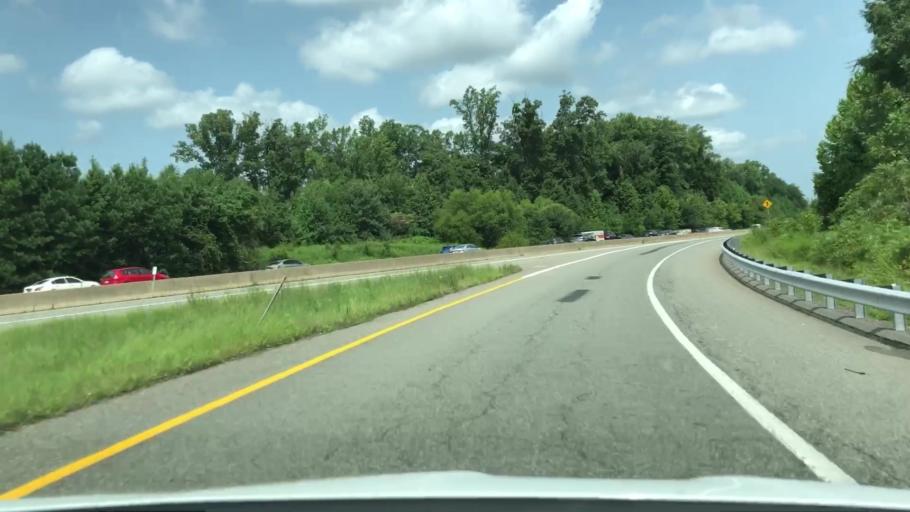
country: US
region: Virginia
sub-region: Henrico County
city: Glen Allen
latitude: 37.6921
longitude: -77.4498
